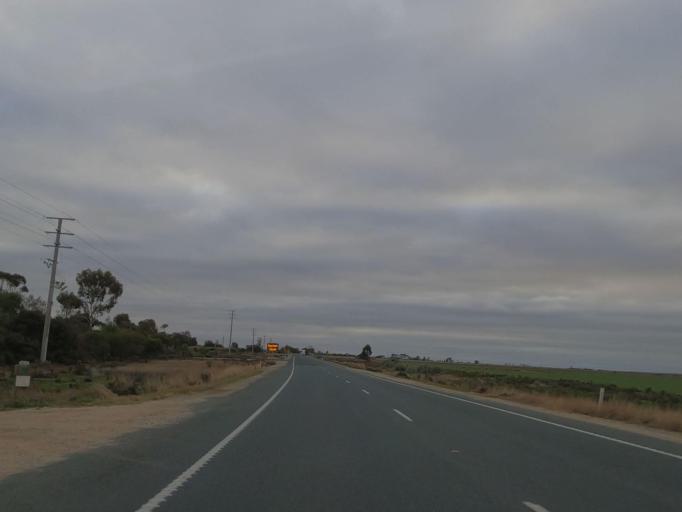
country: AU
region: Victoria
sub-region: Swan Hill
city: Swan Hill
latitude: -35.5547
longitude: 143.7759
